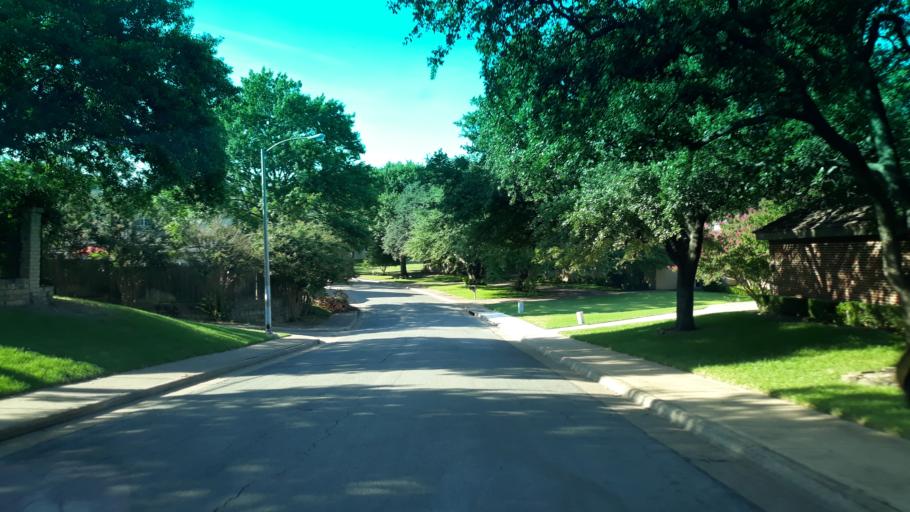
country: US
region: Texas
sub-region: Dallas County
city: Highland Park
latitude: 32.8285
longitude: -96.7474
